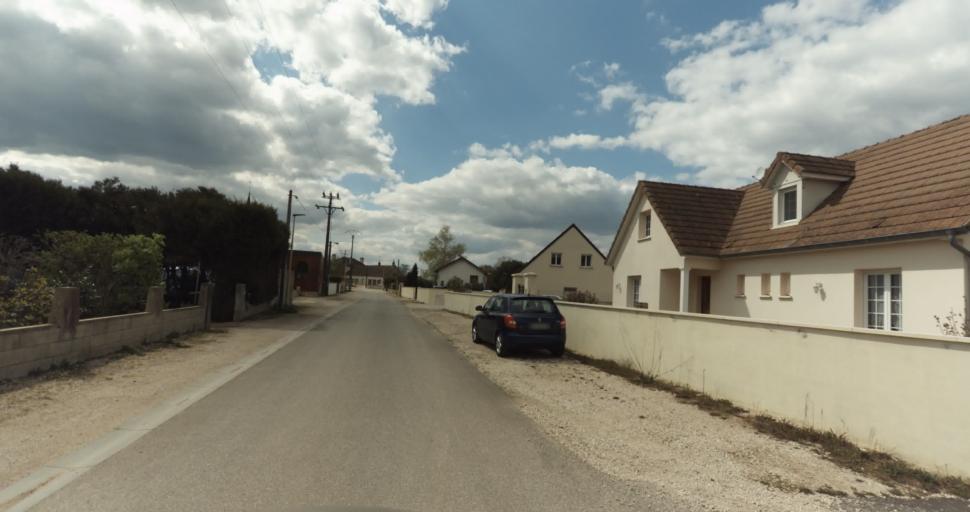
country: FR
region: Bourgogne
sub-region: Departement de la Cote-d'Or
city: Auxonne
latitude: 47.1585
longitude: 5.3832
